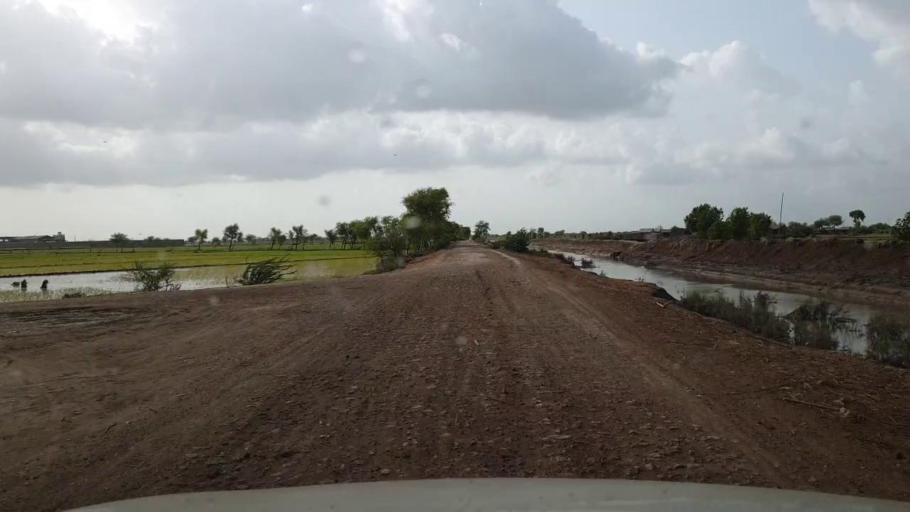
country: PK
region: Sindh
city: Kario
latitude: 24.7752
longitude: 68.5924
